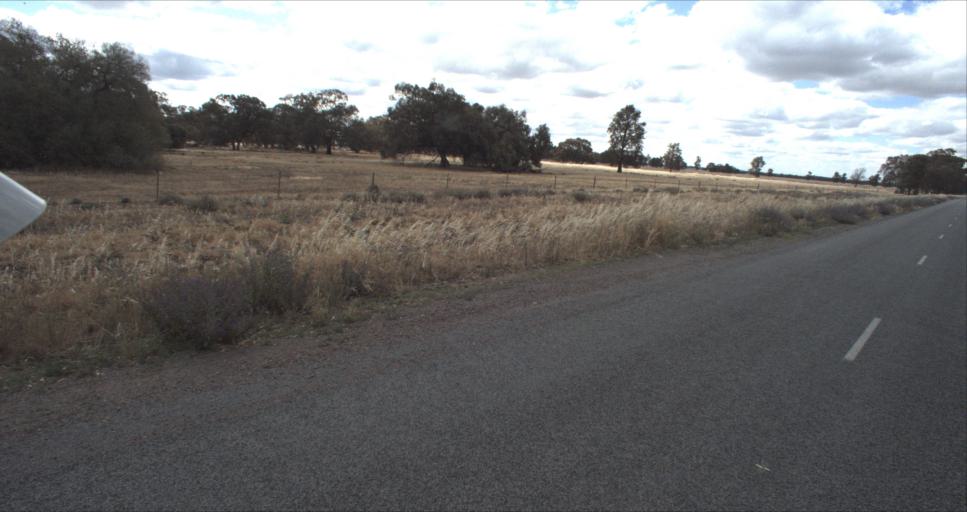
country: AU
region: New South Wales
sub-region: Leeton
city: Leeton
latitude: -34.6900
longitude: 146.3439
